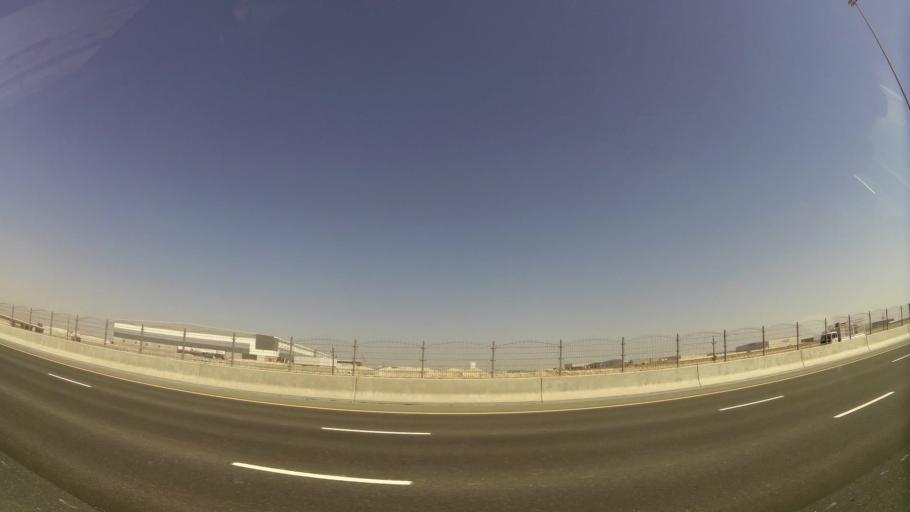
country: AE
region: Dubai
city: Dubai
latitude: 24.9276
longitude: 55.1139
